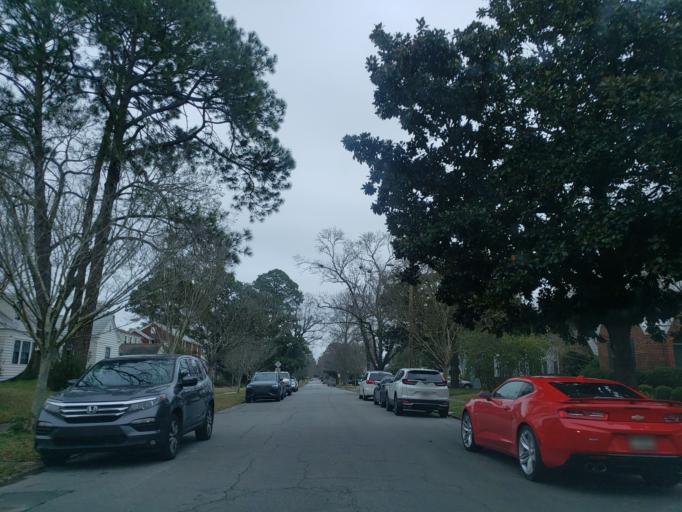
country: US
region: Georgia
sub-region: Chatham County
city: Savannah
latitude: 32.0425
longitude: -81.0952
